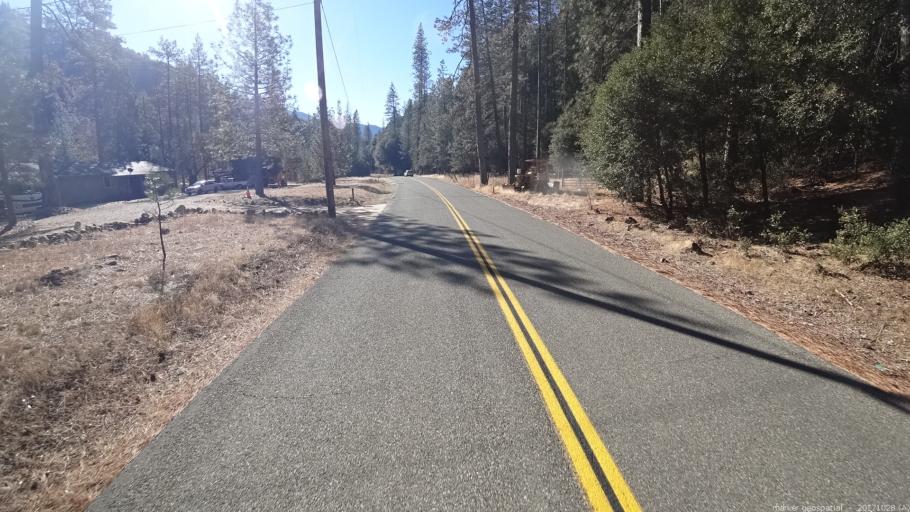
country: US
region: California
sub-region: Trinity County
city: Lewiston
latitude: 40.7799
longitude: -122.6123
